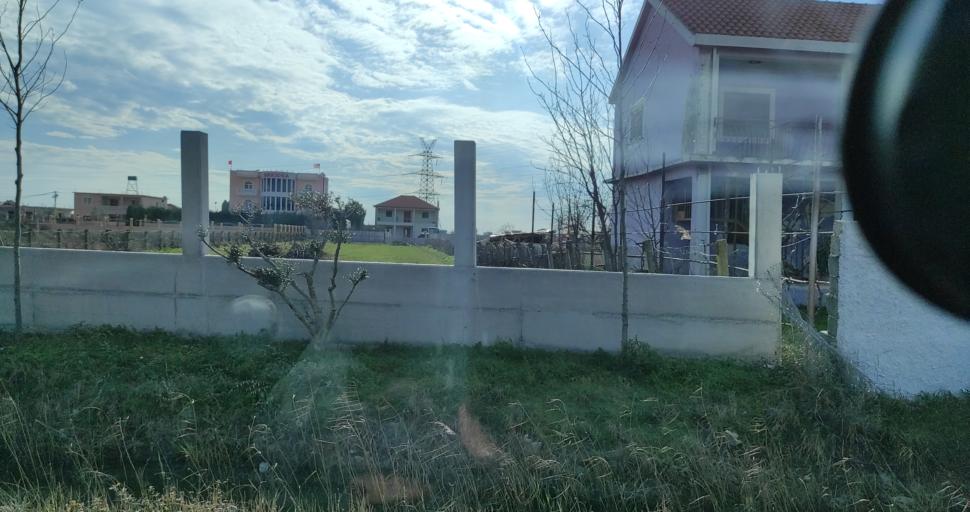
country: AL
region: Lezhe
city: Lezhe
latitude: 41.7844
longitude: 19.6289
